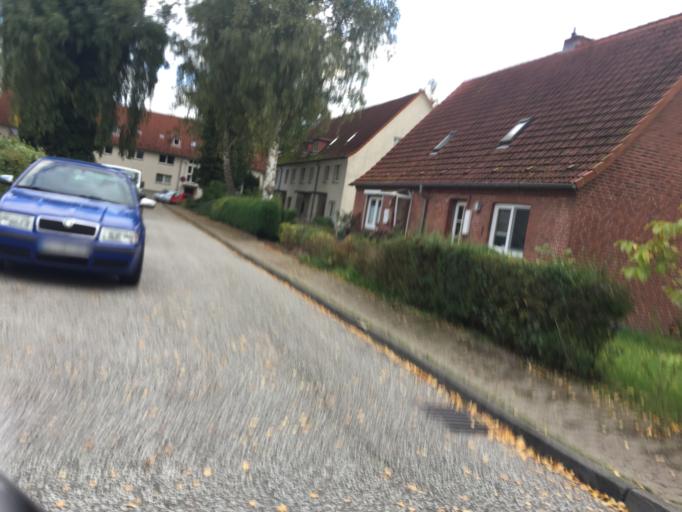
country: DE
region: Schleswig-Holstein
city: Itzehoe
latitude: 53.9364
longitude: 9.5032
